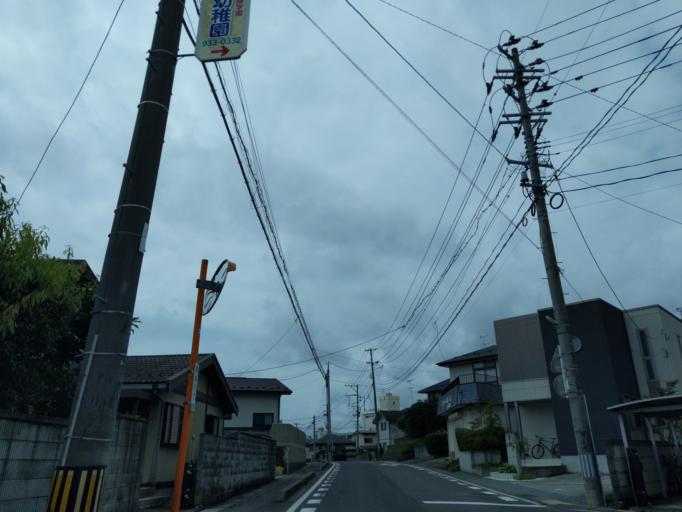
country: JP
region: Fukushima
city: Koriyama
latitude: 37.3893
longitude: 140.3520
